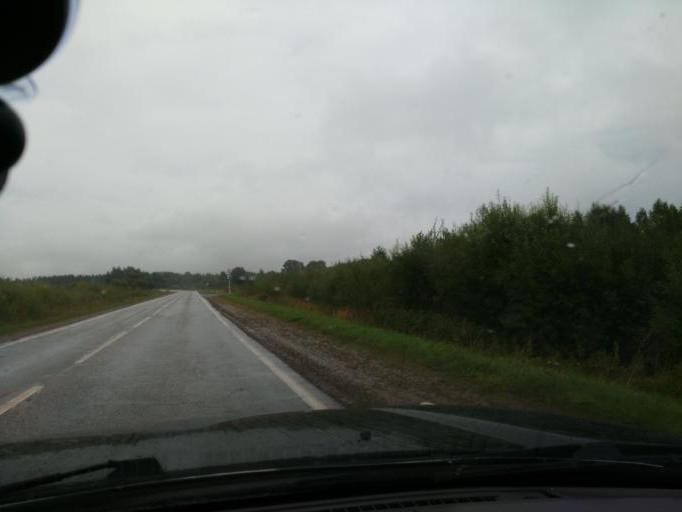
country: RU
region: Perm
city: Osa
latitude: 57.3939
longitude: 55.6140
